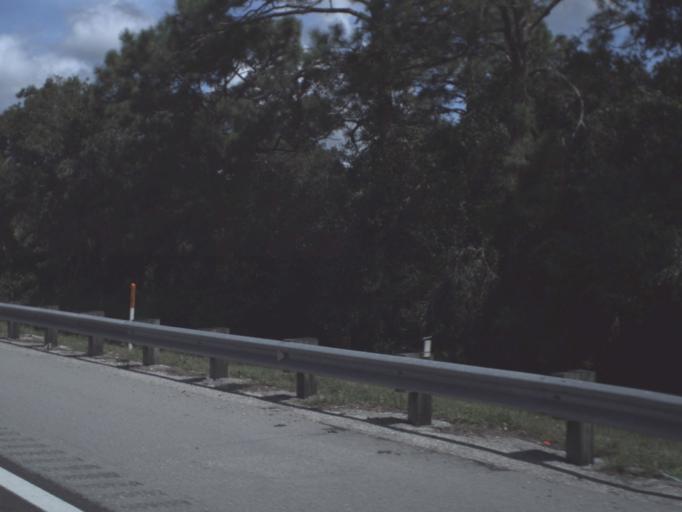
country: US
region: Florida
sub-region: Sarasota County
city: Nokomis
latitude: 27.1487
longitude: -82.4163
